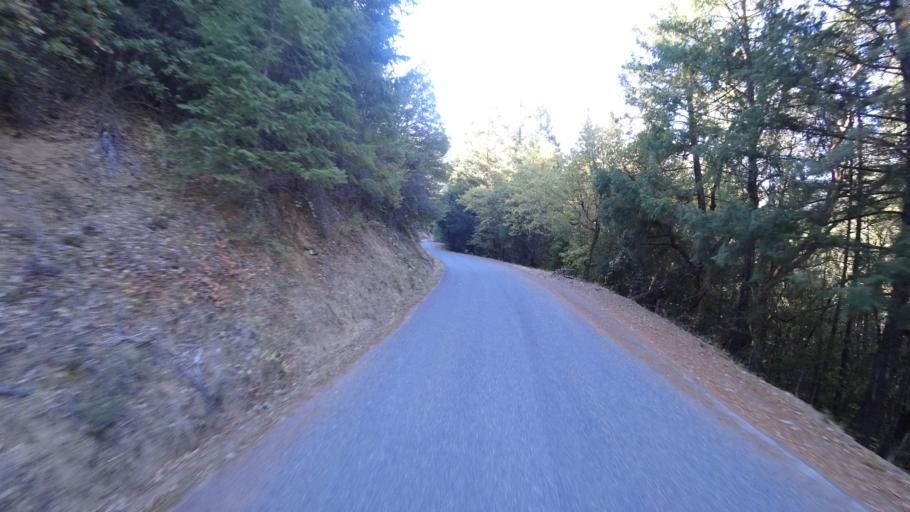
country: US
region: California
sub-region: Humboldt County
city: Willow Creek
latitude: 41.1534
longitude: -123.2090
